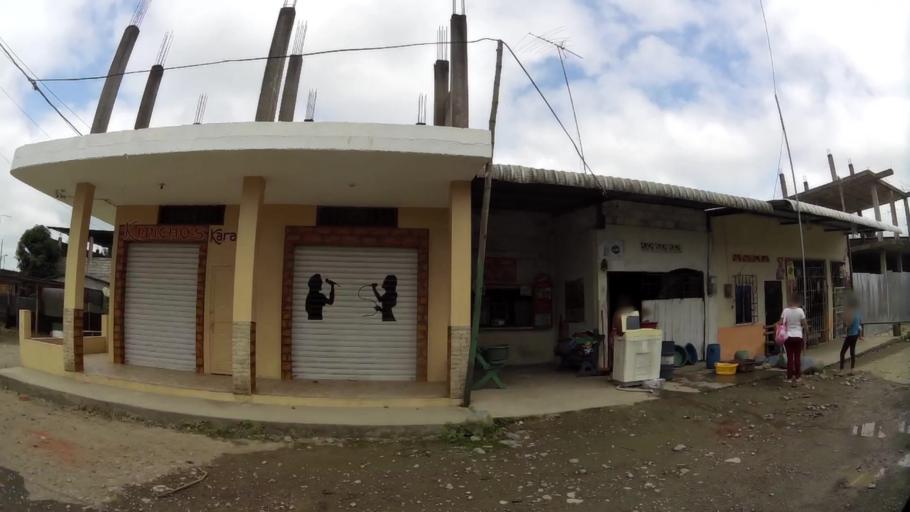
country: EC
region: Guayas
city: Naranjal
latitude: -2.6781
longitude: -79.6278
